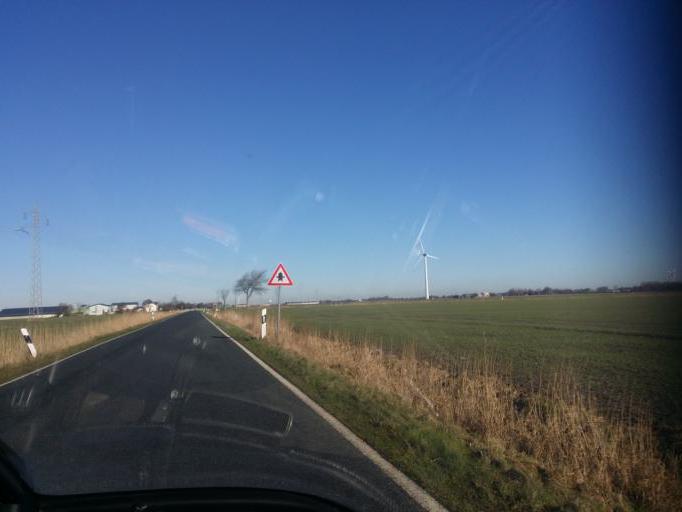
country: DE
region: Schleswig-Holstein
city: Karolinenkoog
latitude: 54.2804
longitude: 8.9604
